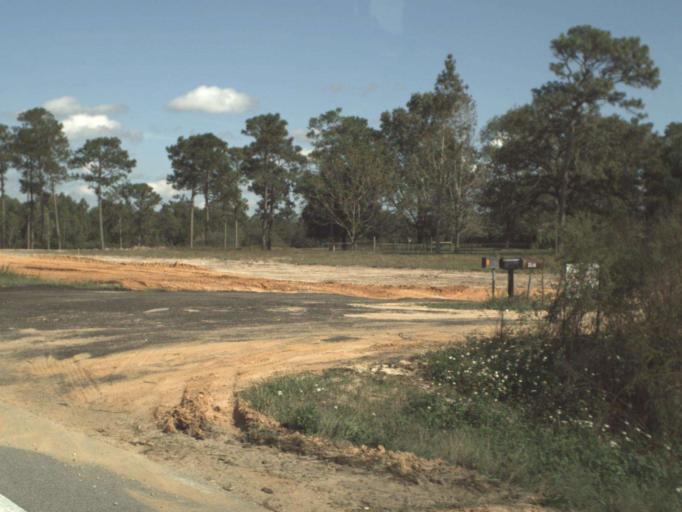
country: US
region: Florida
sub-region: Walton County
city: DeFuniak Springs
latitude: 30.6516
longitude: -86.1146
